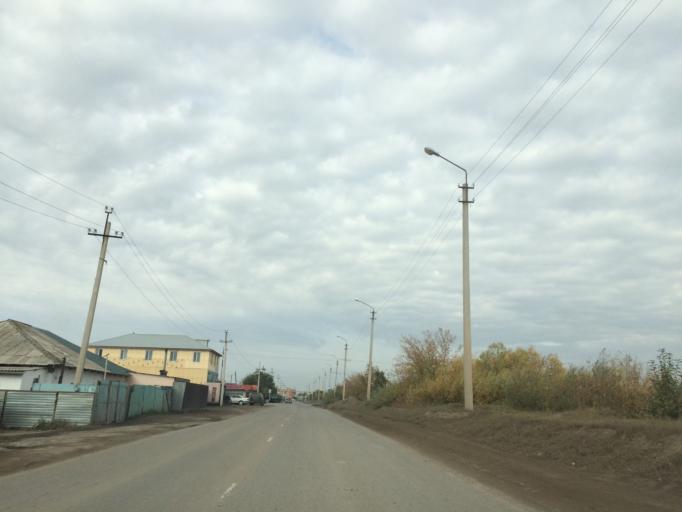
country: KZ
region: Astana Qalasy
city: Astana
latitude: 51.2070
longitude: 71.4104
